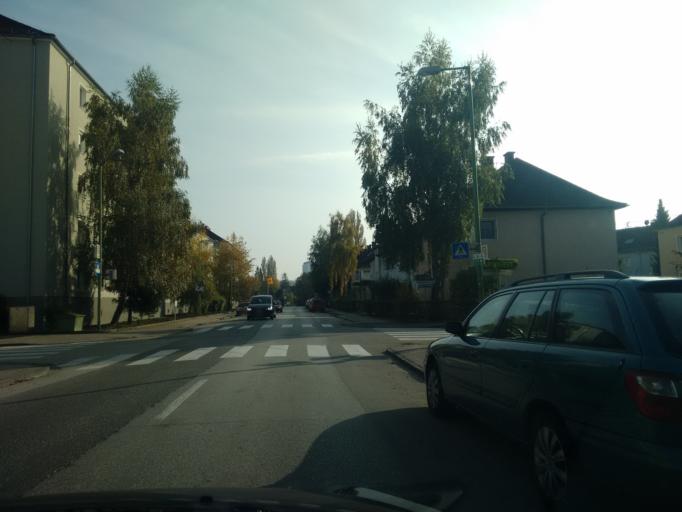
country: AT
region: Upper Austria
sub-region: Wels Stadt
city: Wels
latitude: 48.1646
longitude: 14.0145
